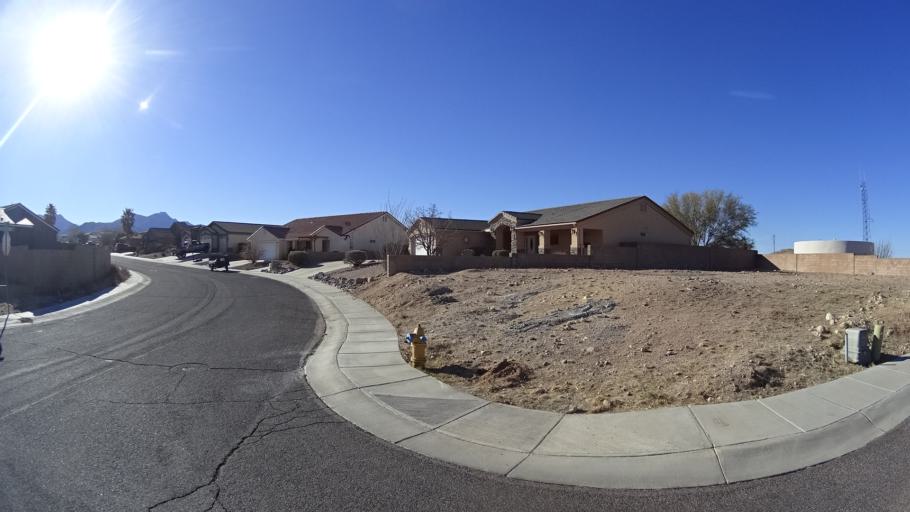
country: US
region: Arizona
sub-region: Mohave County
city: Kingman
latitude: 35.1857
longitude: -114.0022
